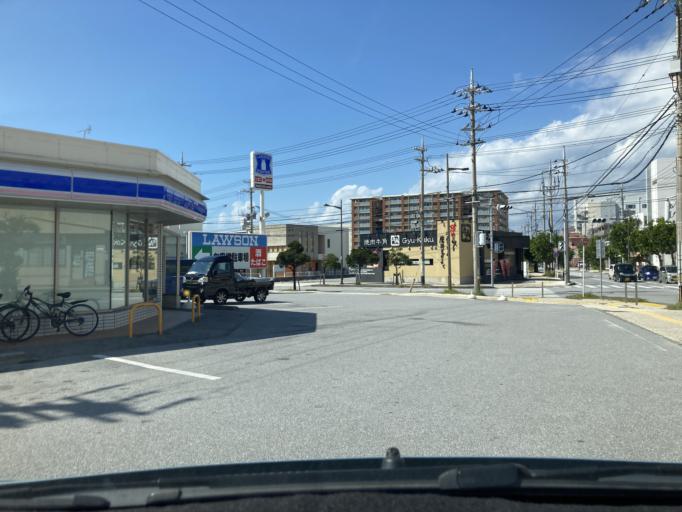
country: JP
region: Okinawa
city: Ginowan
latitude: 26.2735
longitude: 127.7328
